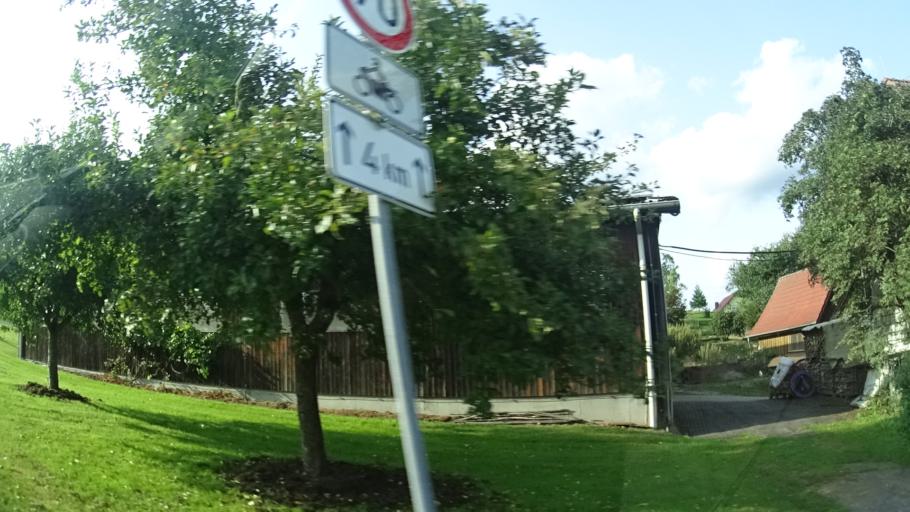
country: DE
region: Hesse
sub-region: Regierungsbezirk Darmstadt
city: Beerfelden
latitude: 49.5498
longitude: 9.0103
